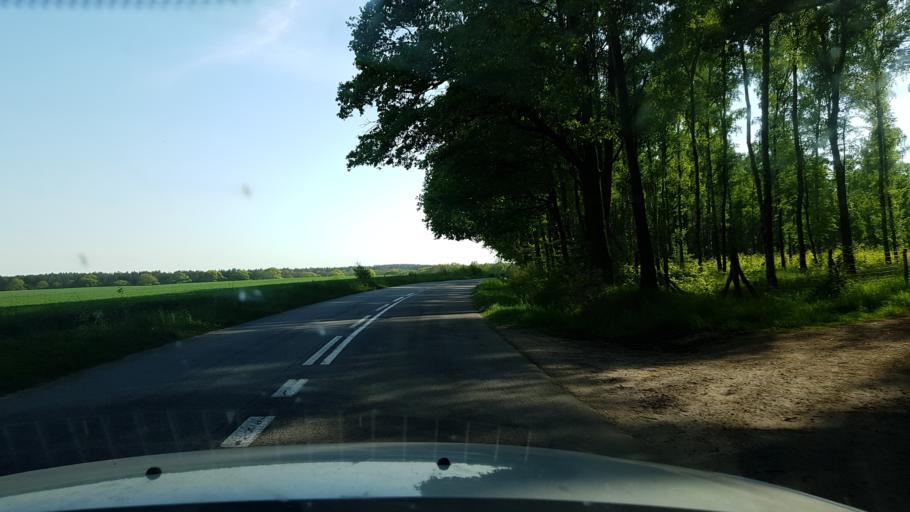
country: PL
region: West Pomeranian Voivodeship
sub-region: Powiat lobeski
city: Resko
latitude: 53.7389
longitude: 15.3613
